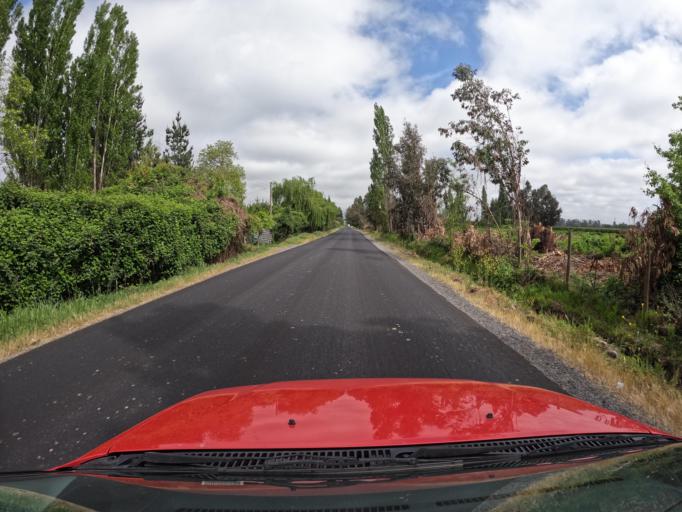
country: CL
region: O'Higgins
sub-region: Provincia de Colchagua
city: Santa Cruz
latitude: -34.6778
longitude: -71.3637
